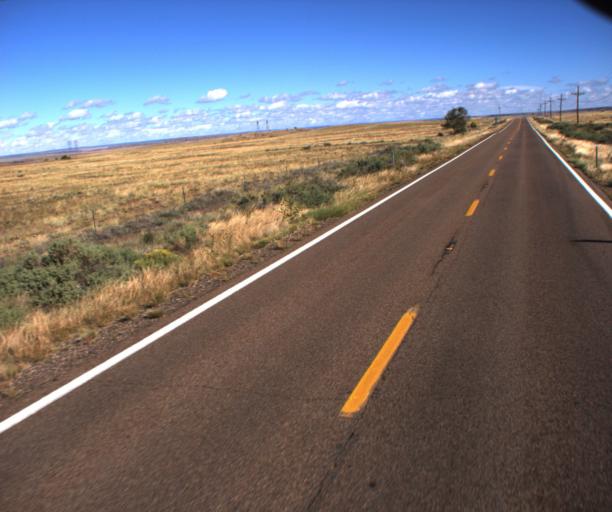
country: US
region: Arizona
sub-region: Apache County
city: Saint Johns
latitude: 34.5641
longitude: -109.3403
